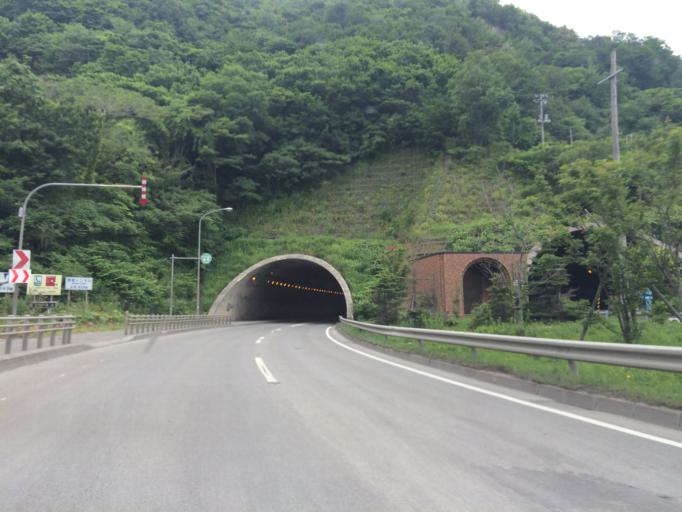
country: JP
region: Hokkaido
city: Otaru
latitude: 43.1622
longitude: 141.0995
